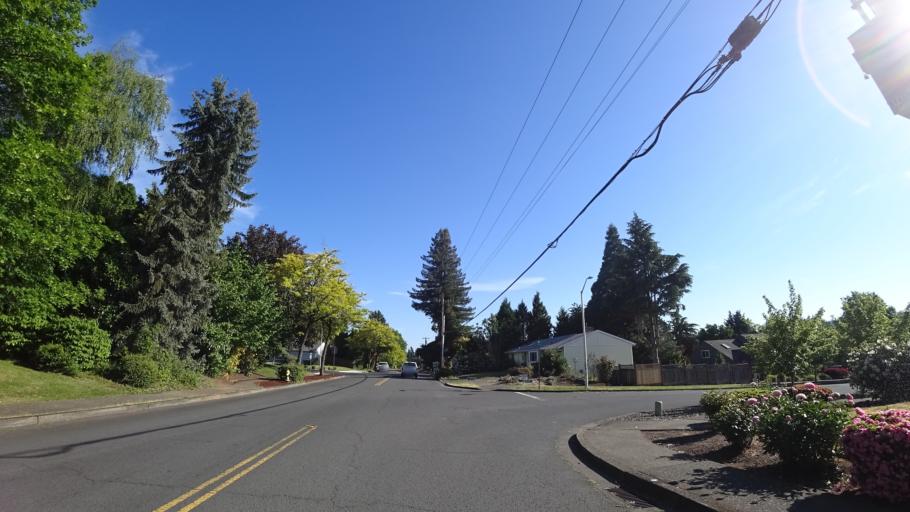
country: US
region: Oregon
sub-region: Washington County
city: Beaverton
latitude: 45.4586
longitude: -122.8080
